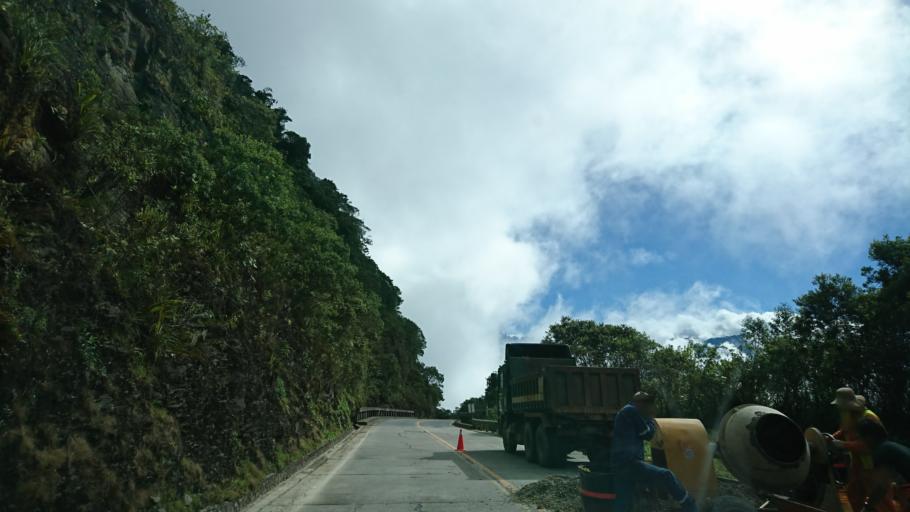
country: BO
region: La Paz
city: Coroico
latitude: -16.2266
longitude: -67.8284
